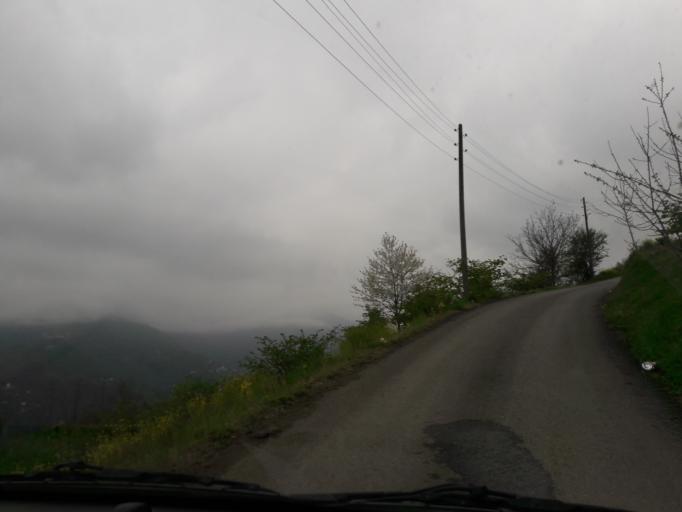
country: TR
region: Trabzon
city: Duzkoy
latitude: 40.9316
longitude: 39.4778
